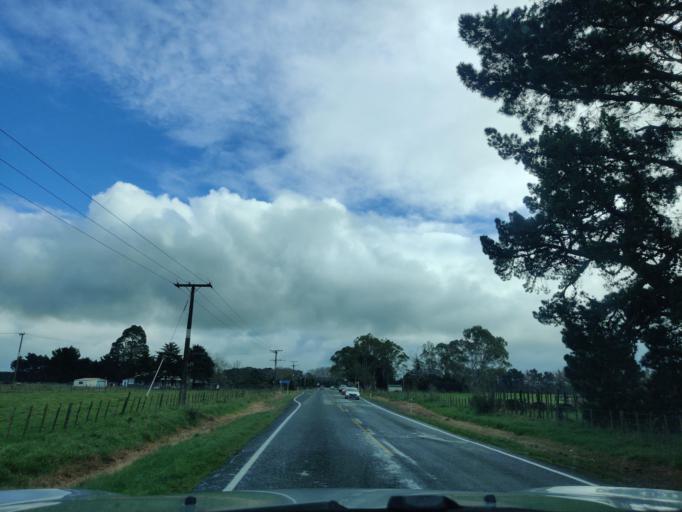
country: NZ
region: Hawke's Bay
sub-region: Hastings District
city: Hastings
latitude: -40.0211
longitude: 176.3355
